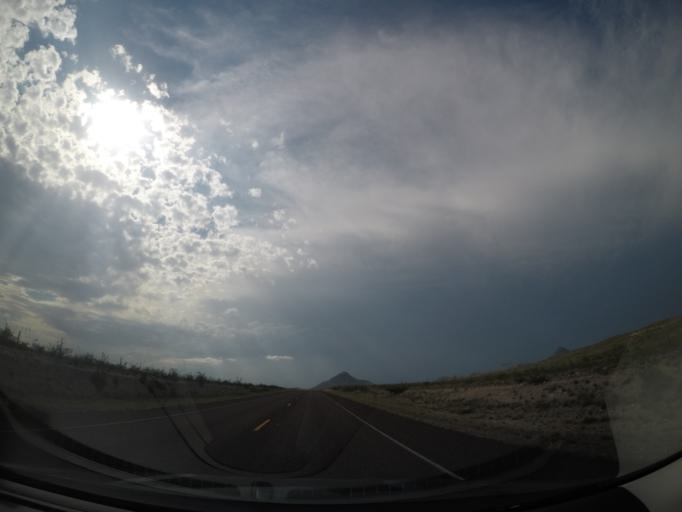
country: US
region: Texas
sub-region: Brewster County
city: Alpine
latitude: 29.8099
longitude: -103.1975
